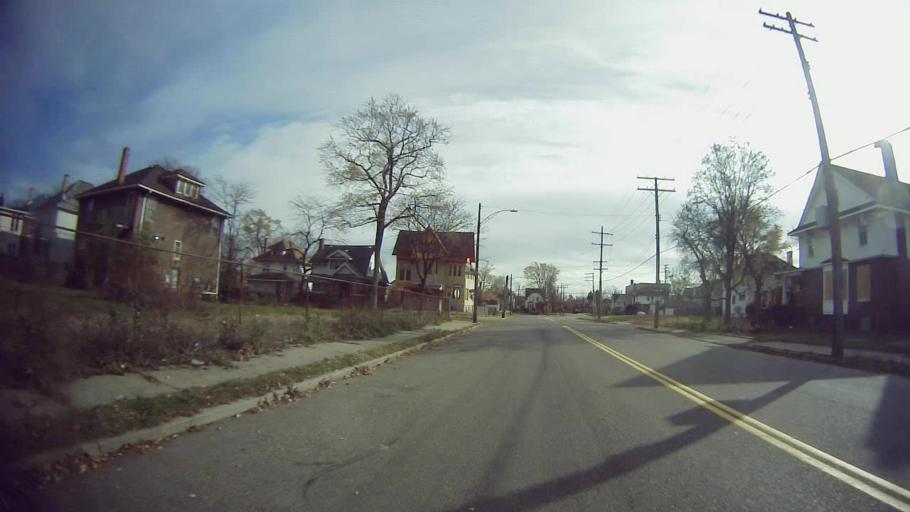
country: US
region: Michigan
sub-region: Wayne County
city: Hamtramck
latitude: 42.3846
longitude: -83.0753
